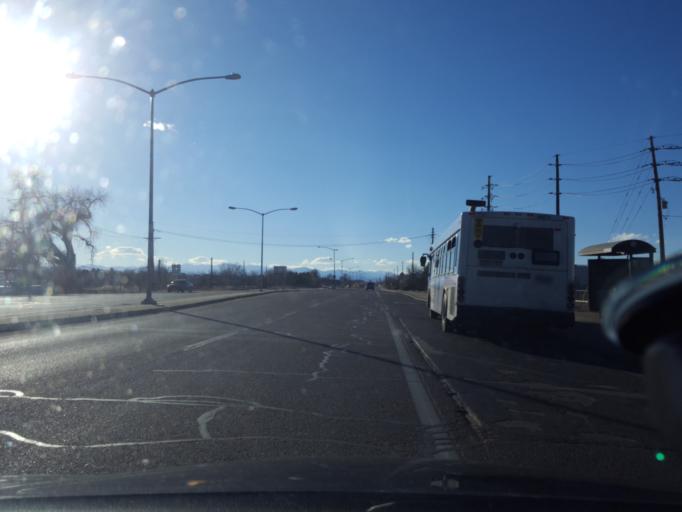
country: US
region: Colorado
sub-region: Adams County
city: Aurora
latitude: 39.7403
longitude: -104.7731
